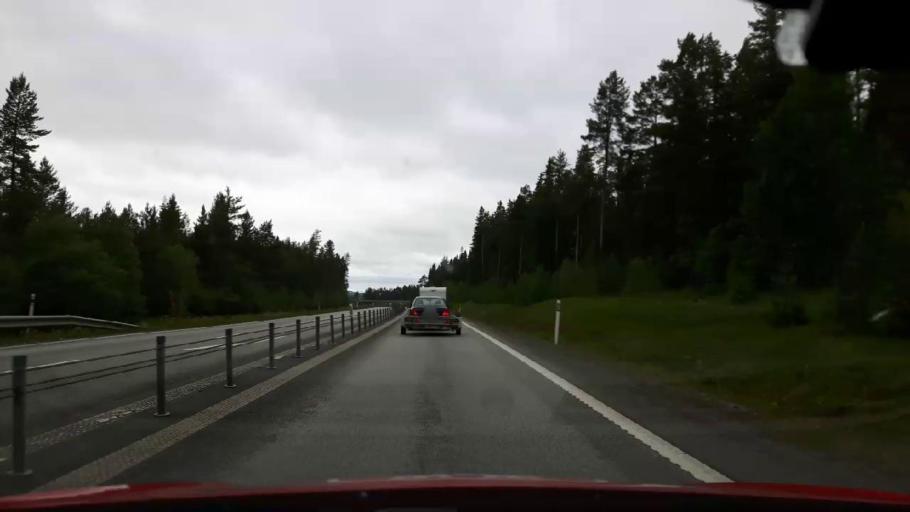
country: SE
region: Jaemtland
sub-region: OEstersunds Kommun
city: Ostersund
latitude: 63.1995
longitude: 14.6831
